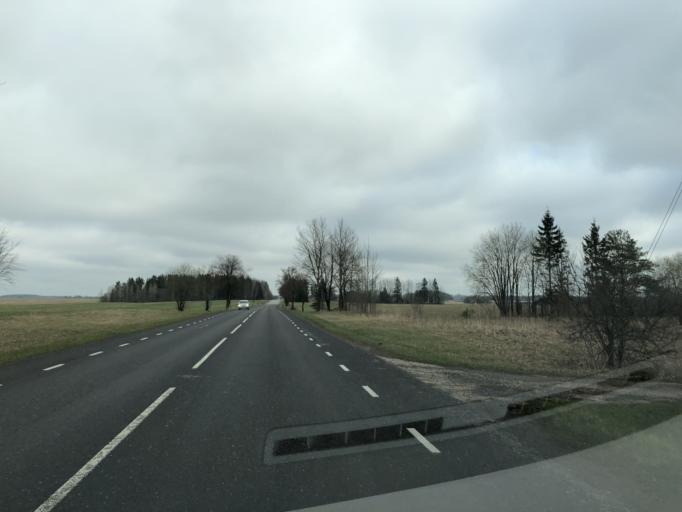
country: EE
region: Laeaene-Virumaa
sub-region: Rakvere linn
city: Rakvere
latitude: 59.2893
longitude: 26.3068
